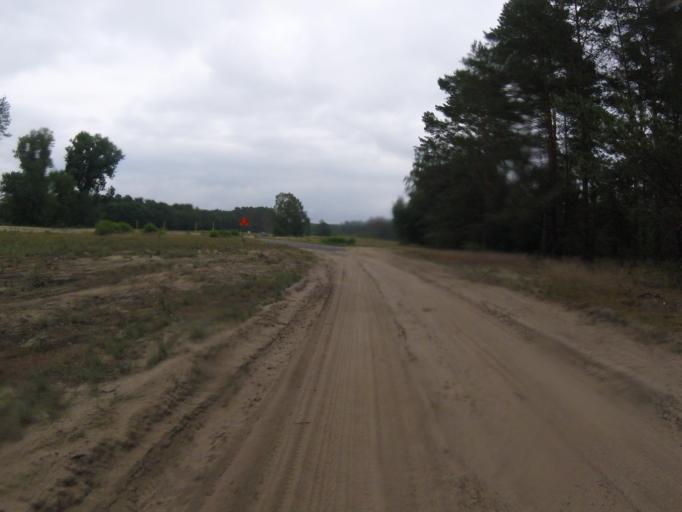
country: DE
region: Brandenburg
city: Gross Koris
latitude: 52.1924
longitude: 13.6434
